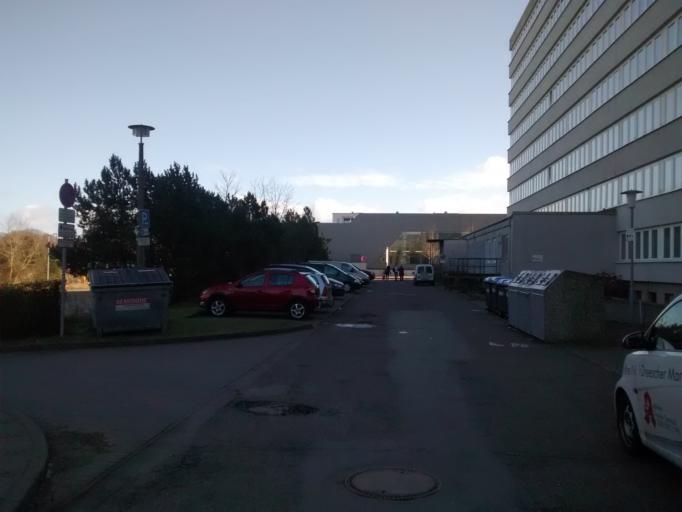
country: DE
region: Mecklenburg-Vorpommern
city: Altstadt
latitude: 53.6039
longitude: 11.4325
